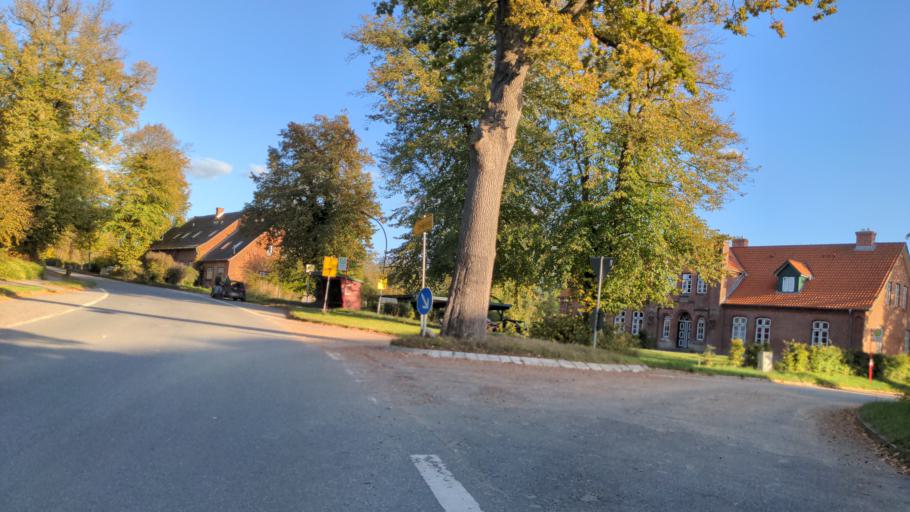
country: DE
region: Schleswig-Holstein
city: Pronstorf
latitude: 53.9572
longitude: 10.4685
